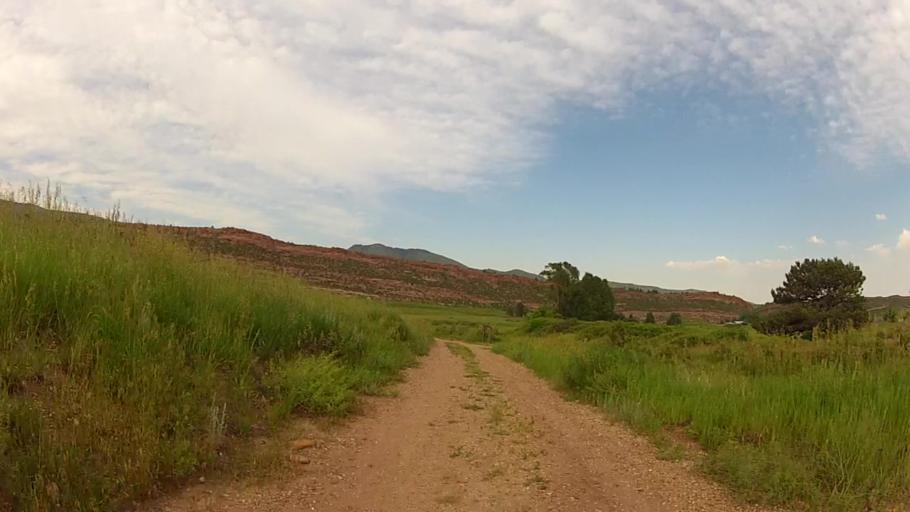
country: US
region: Colorado
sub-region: Larimer County
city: Laporte
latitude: 40.4860
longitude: -105.2329
